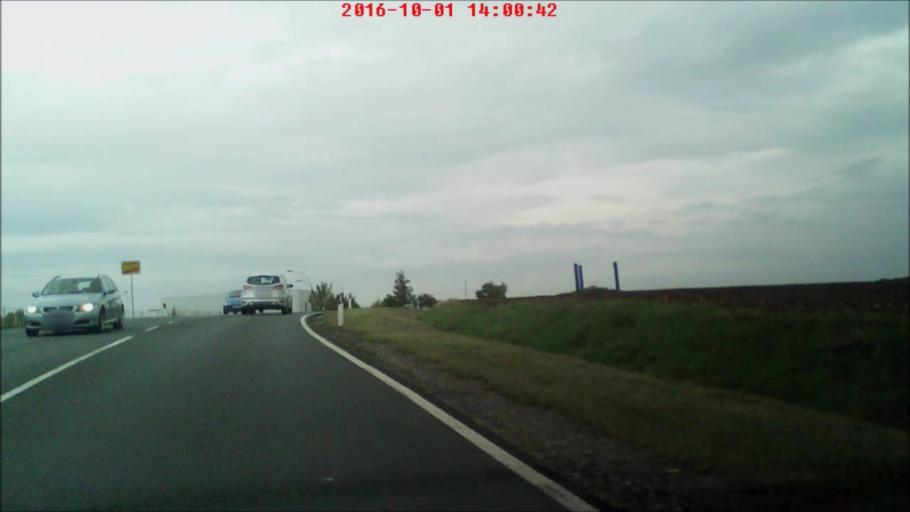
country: DE
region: Thuringia
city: Umpferstedt
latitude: 50.9778
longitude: 11.4183
